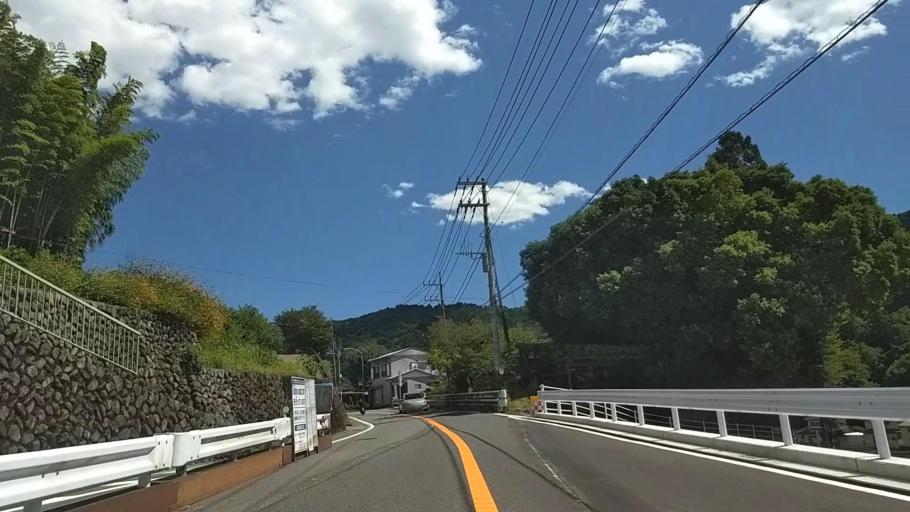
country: JP
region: Tokyo
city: Hachioji
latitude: 35.5667
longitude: 139.2681
